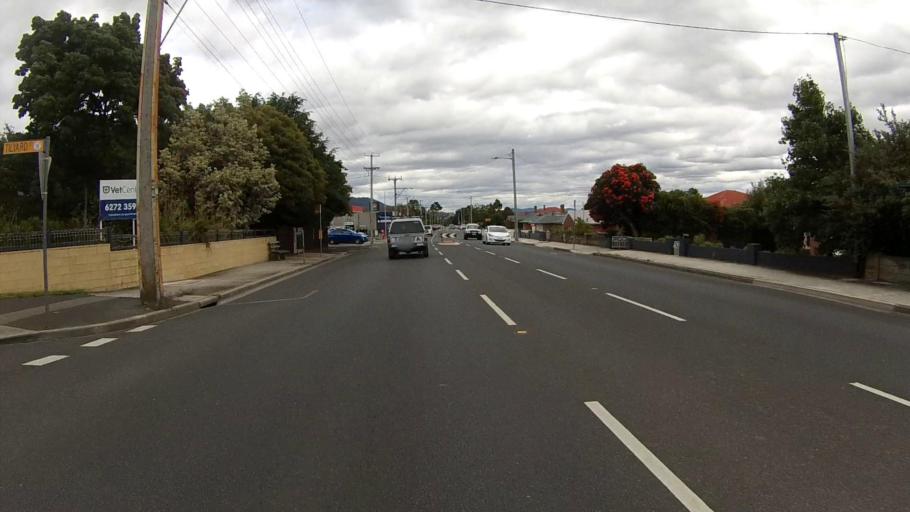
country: AU
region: Tasmania
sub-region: Glenorchy
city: Glenorchy
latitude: -42.8265
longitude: 147.2666
